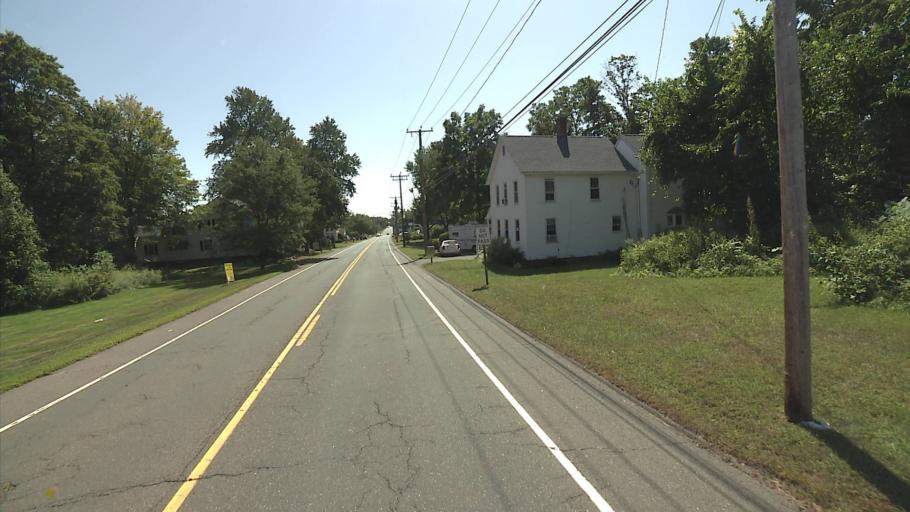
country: US
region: Connecticut
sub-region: Hartford County
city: Windsor Locks
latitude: 41.9517
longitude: -72.6277
